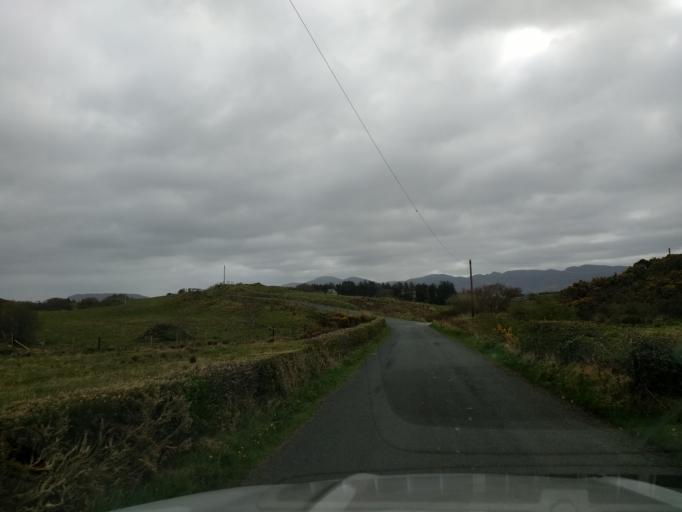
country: IE
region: Ulster
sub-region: County Donegal
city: Ramelton
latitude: 55.2509
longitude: -7.6334
